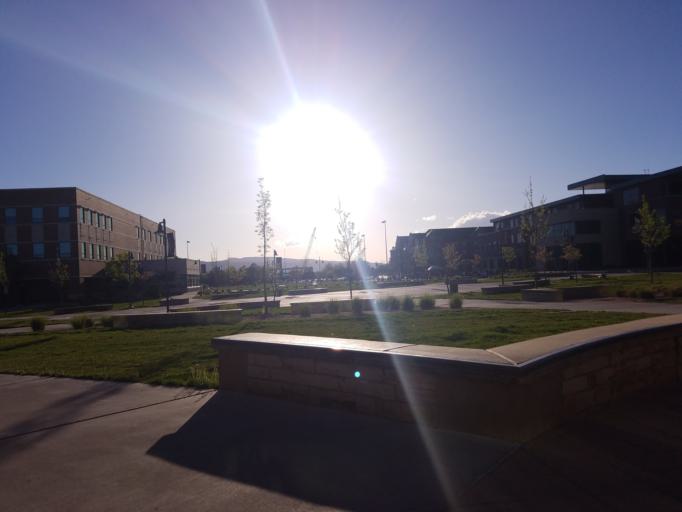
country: US
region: Colorado
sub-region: Mesa County
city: Grand Junction
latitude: 39.0807
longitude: -108.5542
